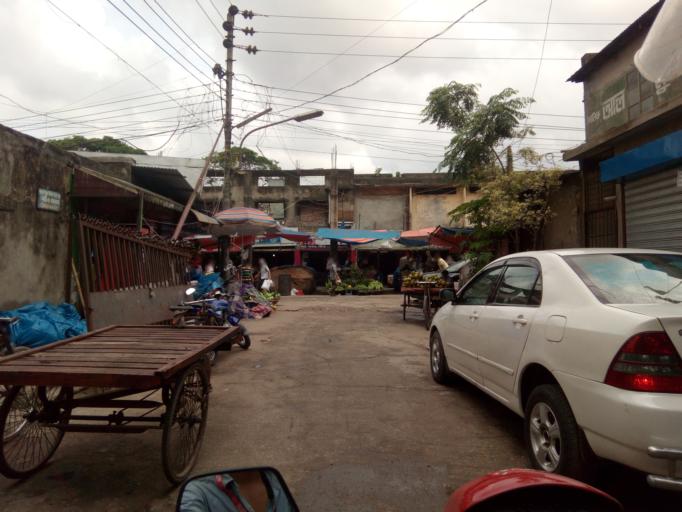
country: BD
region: Dhaka
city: Azimpur
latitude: 23.7604
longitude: 90.3658
